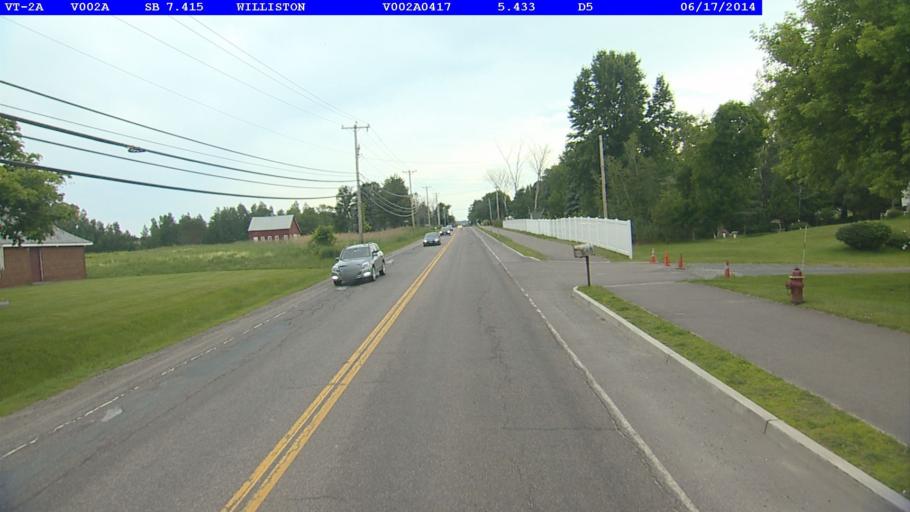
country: US
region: Vermont
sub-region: Chittenden County
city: Essex Junction
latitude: 44.4743
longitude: -73.1133
